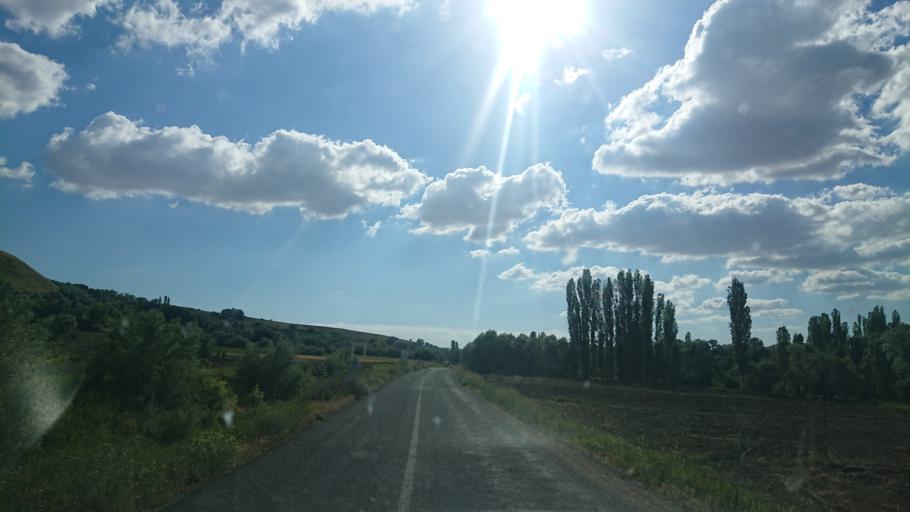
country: TR
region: Aksaray
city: Agacoren
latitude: 38.7572
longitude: 33.8895
